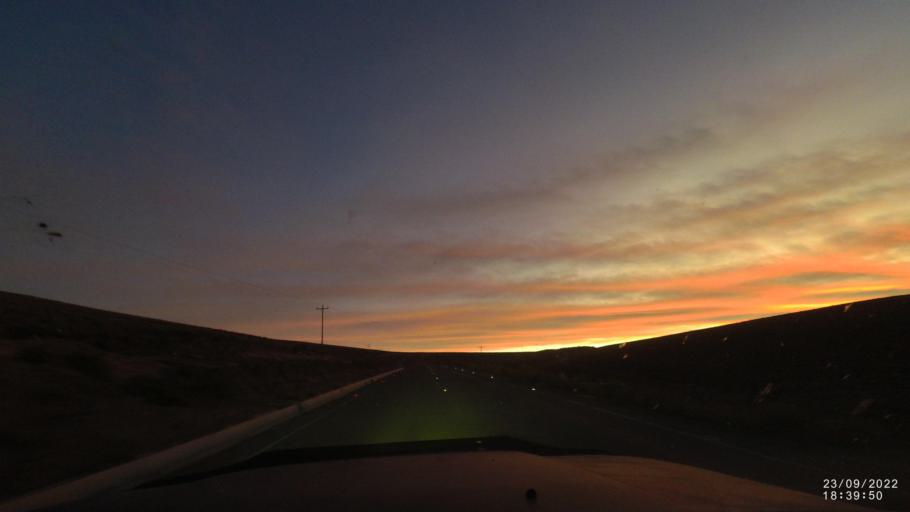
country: BO
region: Oruro
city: Challapata
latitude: -19.4214
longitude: -67.3340
